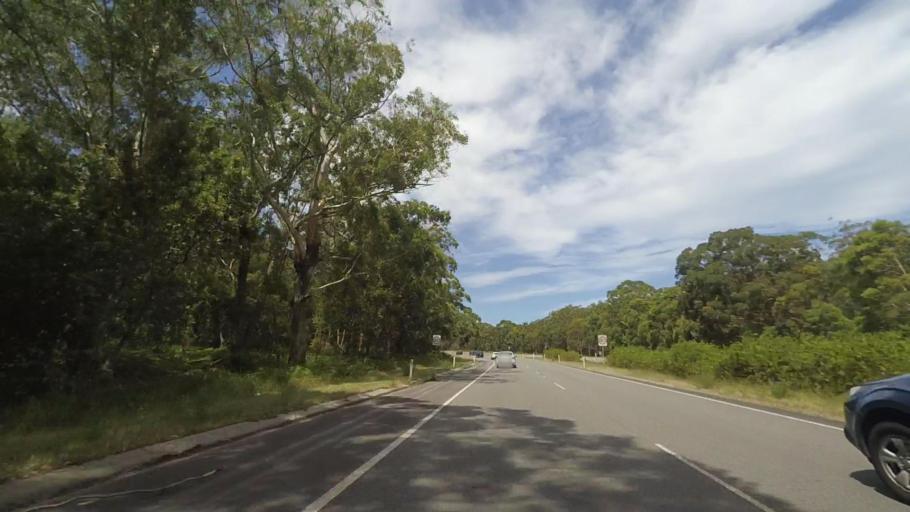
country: AU
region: New South Wales
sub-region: Port Stephens Shire
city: Anna Bay
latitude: -32.7729
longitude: 152.0090
